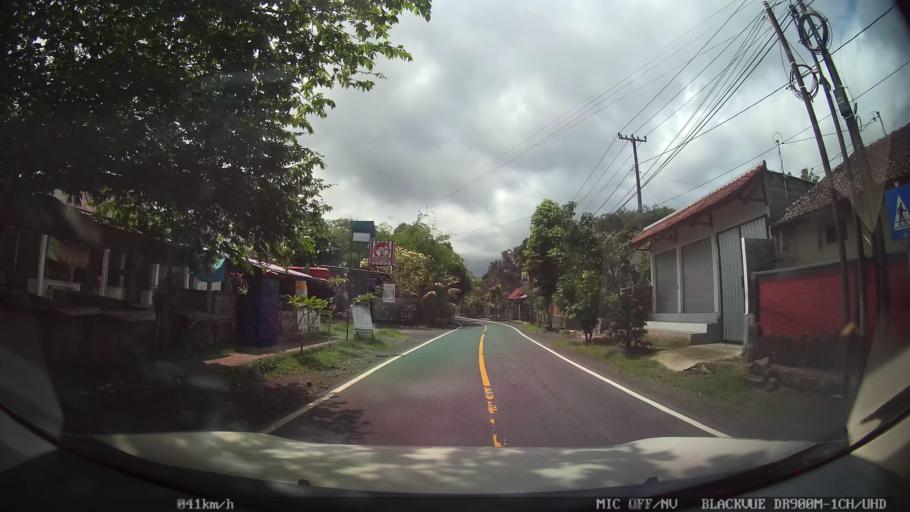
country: ID
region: Bali
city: Banjar Wangsian
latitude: -8.4970
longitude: 115.4032
